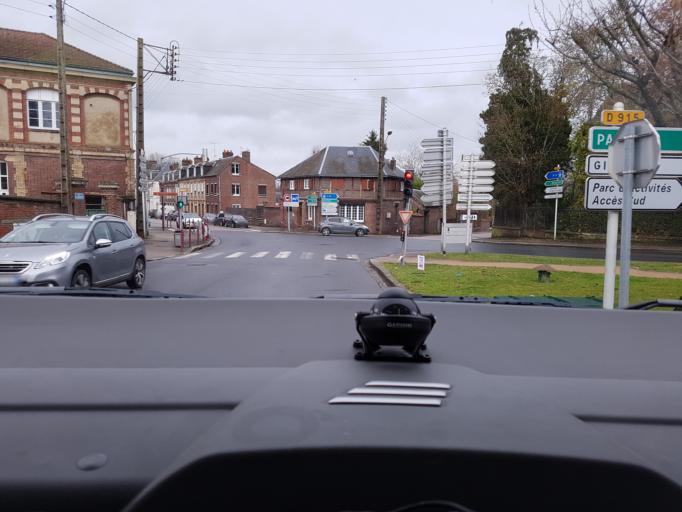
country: FR
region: Haute-Normandie
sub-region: Departement de la Seine-Maritime
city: Gournay-en-Bray
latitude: 49.4792
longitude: 1.7234
